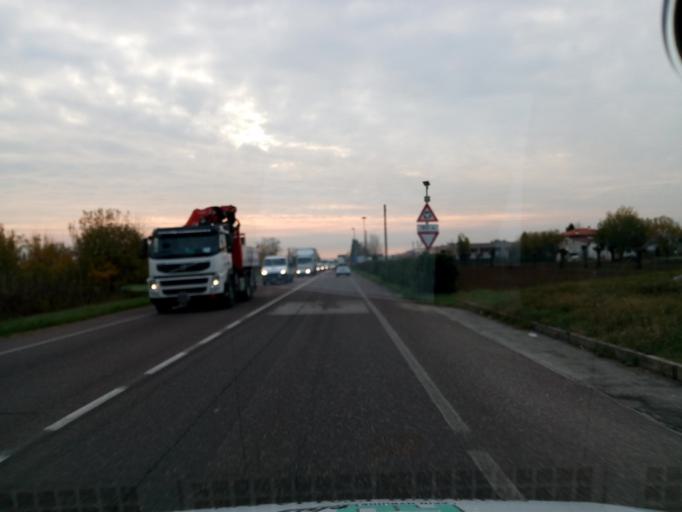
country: IT
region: Veneto
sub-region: Provincia di Vicenza
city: Thiene
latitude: 45.6944
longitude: 11.4637
